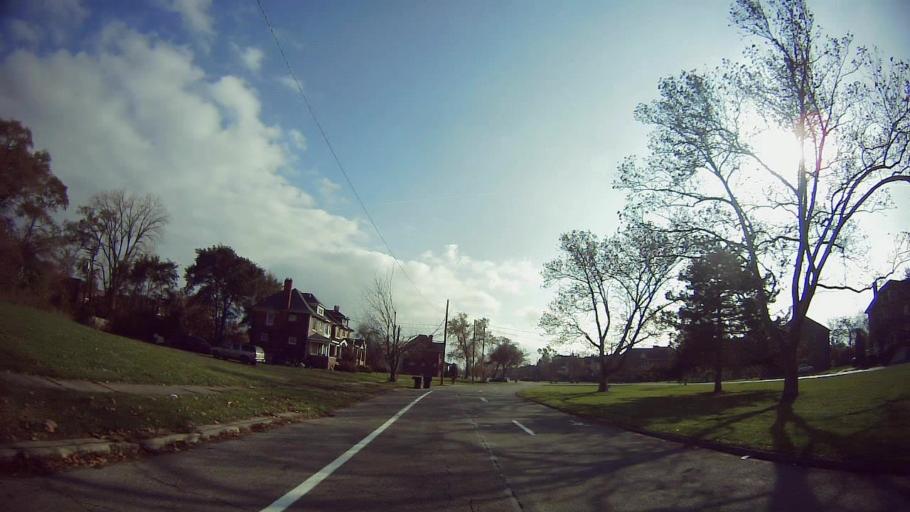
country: US
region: Michigan
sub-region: Wayne County
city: Detroit
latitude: 42.3426
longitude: -83.1060
